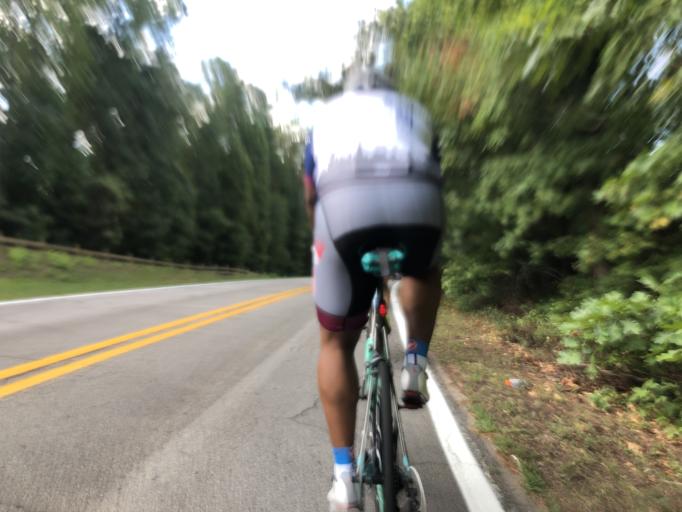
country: US
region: Georgia
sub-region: Fulton County
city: Palmetto
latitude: 33.5776
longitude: -84.6491
